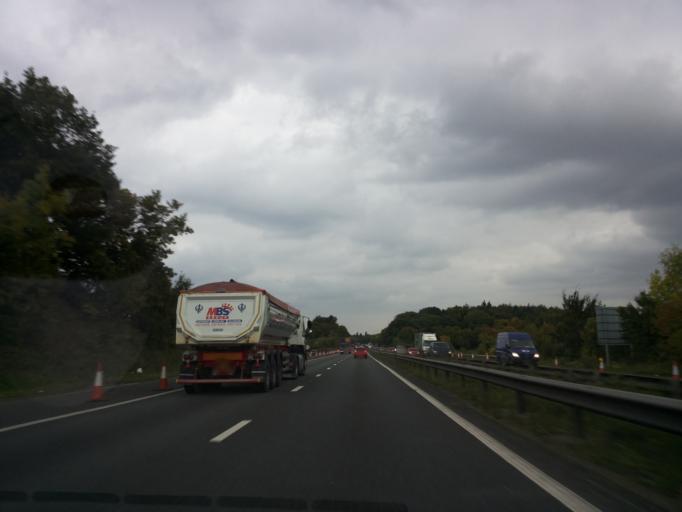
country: GB
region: England
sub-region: Kent
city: Sittingbourne
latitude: 51.3040
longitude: 0.7239
